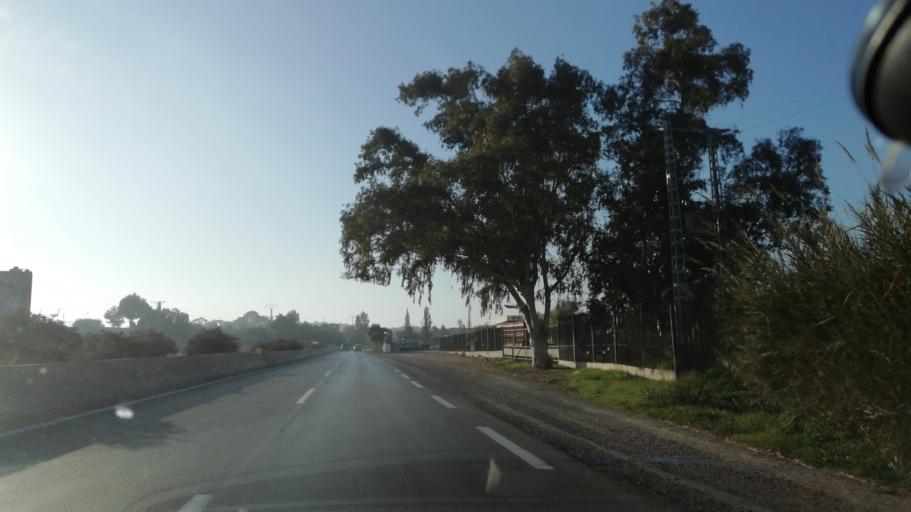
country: DZ
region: Tlemcen
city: Remchi
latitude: 35.1105
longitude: -1.4398
